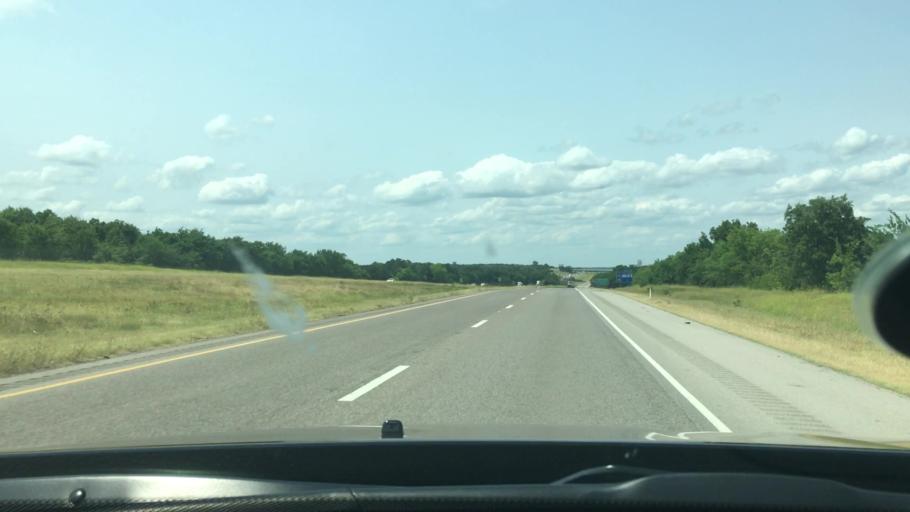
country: US
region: Oklahoma
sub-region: Murray County
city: Davis
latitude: 34.4926
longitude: -97.1643
